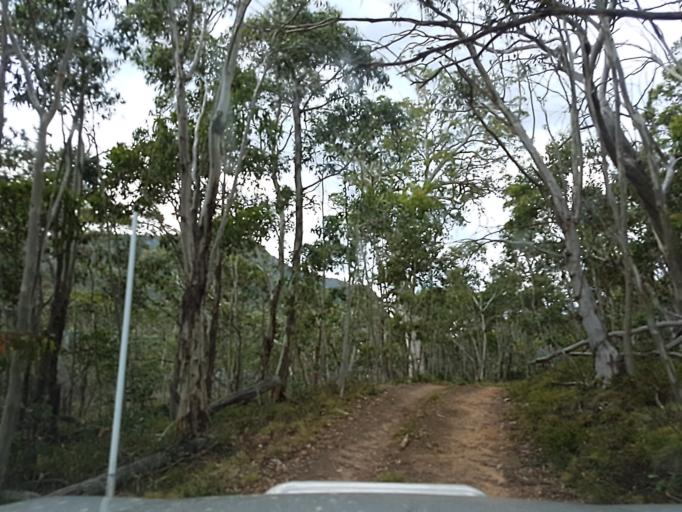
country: AU
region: New South Wales
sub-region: Snowy River
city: Jindabyne
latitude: -36.8845
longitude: 148.1466
